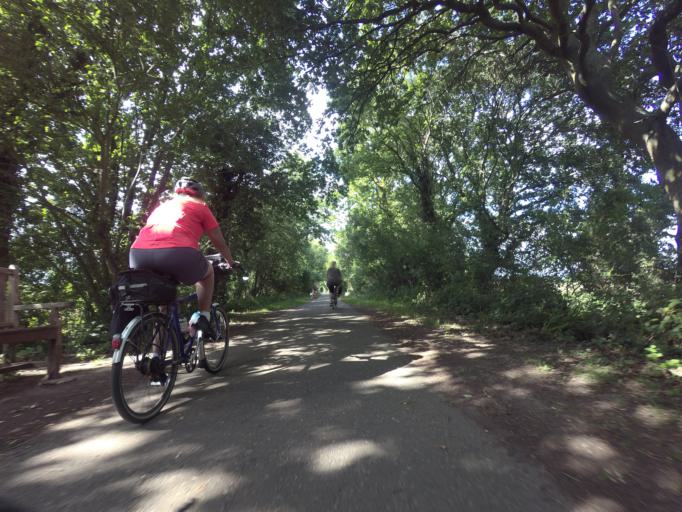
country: GB
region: England
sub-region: East Sussex
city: Hailsham
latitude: 50.8506
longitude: 0.2574
